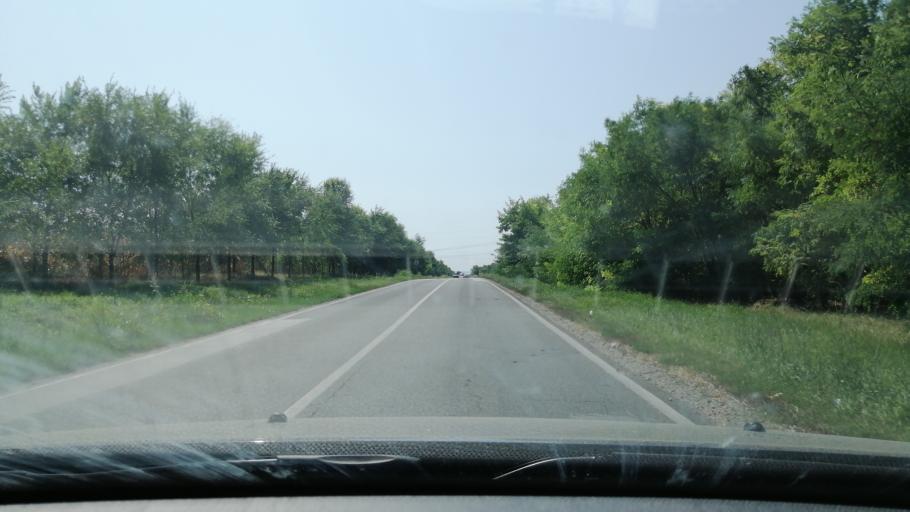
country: RS
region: Autonomna Pokrajina Vojvodina
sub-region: Juznobanatski Okrug
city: Pancevo
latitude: 44.7905
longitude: 20.7237
